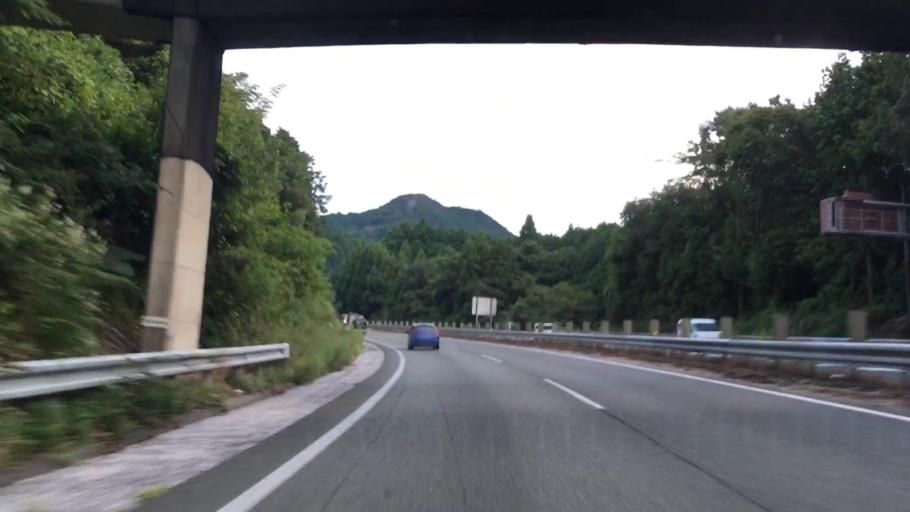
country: JP
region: Yamaguchi
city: Ogori-shimogo
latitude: 34.1670
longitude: 131.2410
